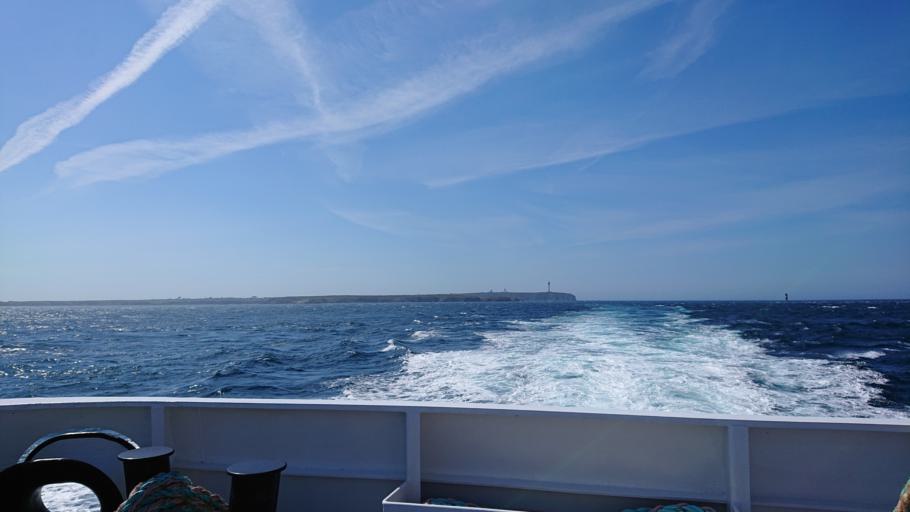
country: FR
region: Brittany
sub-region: Departement du Finistere
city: Porspoder
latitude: 48.4524
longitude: -5.0092
